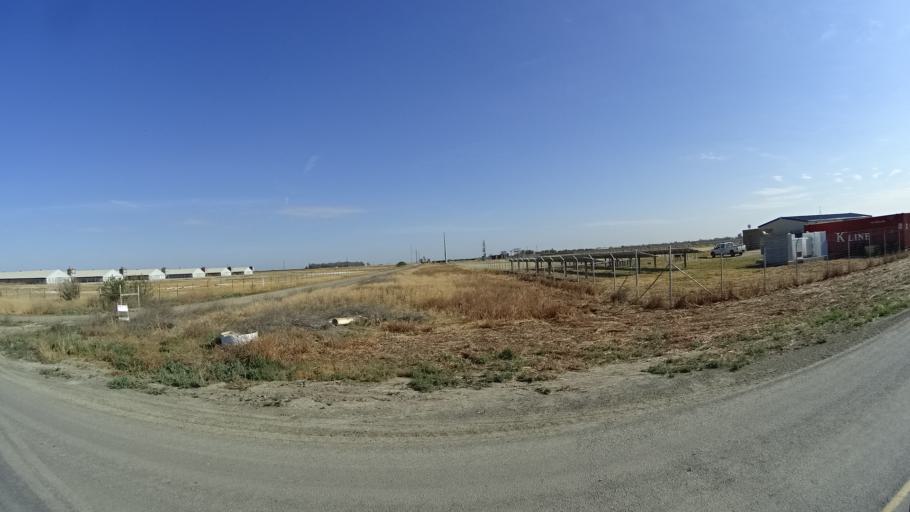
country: US
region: California
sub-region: Kings County
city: Stratford
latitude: 36.2260
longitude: -119.8071
